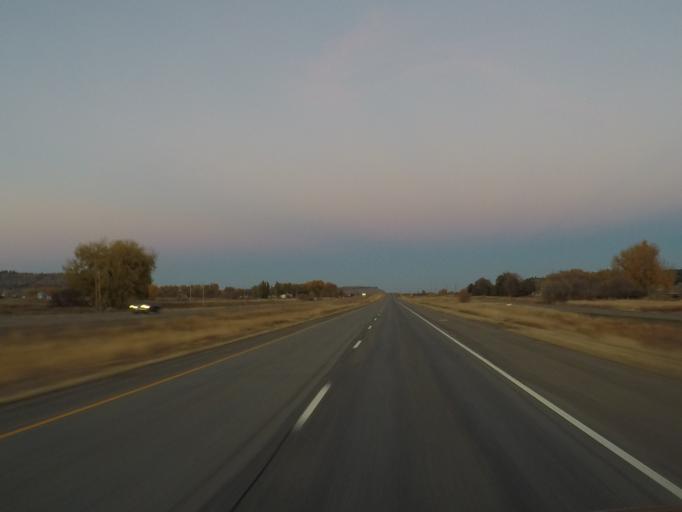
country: US
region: Montana
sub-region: Stillwater County
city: Columbus
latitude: 45.6092
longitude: -109.0188
